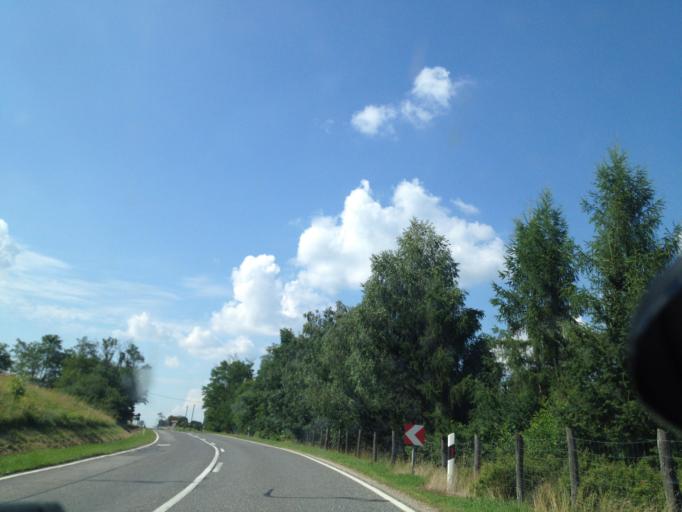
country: HU
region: Veszprem
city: Ajka
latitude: 47.2311
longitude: 17.5946
